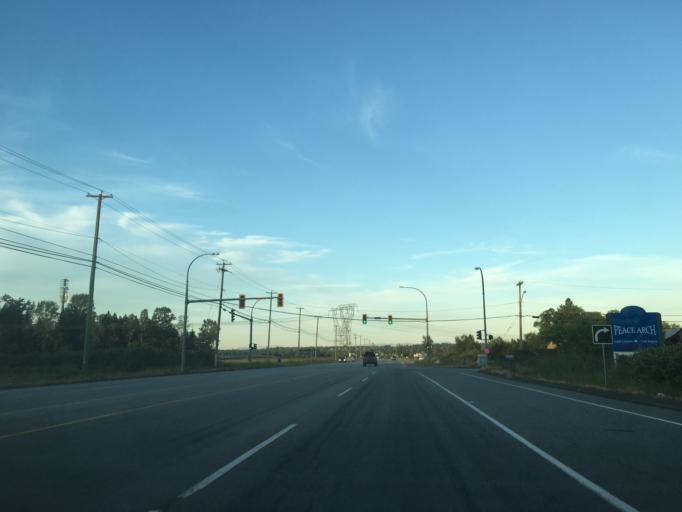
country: US
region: Washington
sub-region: Whatcom County
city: Blaine
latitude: 49.0166
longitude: -122.7474
